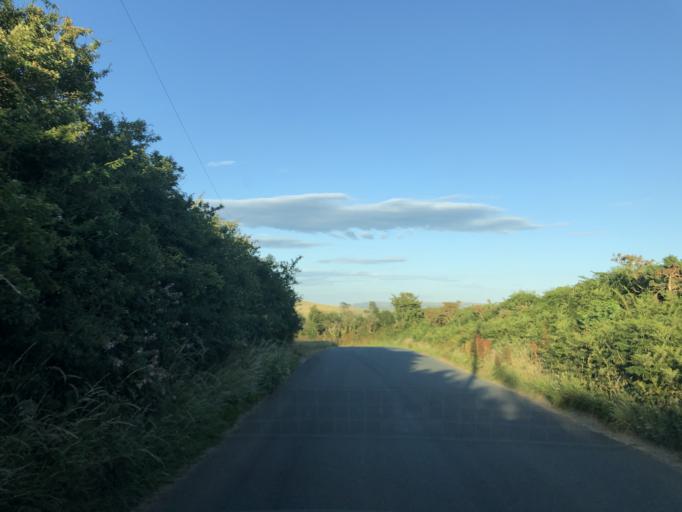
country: GB
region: England
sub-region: Isle of Wight
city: Chale
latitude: 50.6376
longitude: -1.3449
